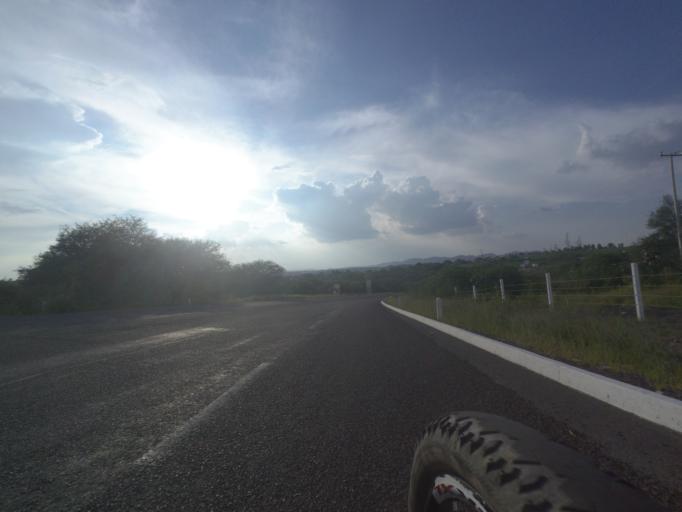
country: MX
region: Aguascalientes
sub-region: Aguascalientes
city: Penuelas (El Cienegal)
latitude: 21.7673
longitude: -102.3570
